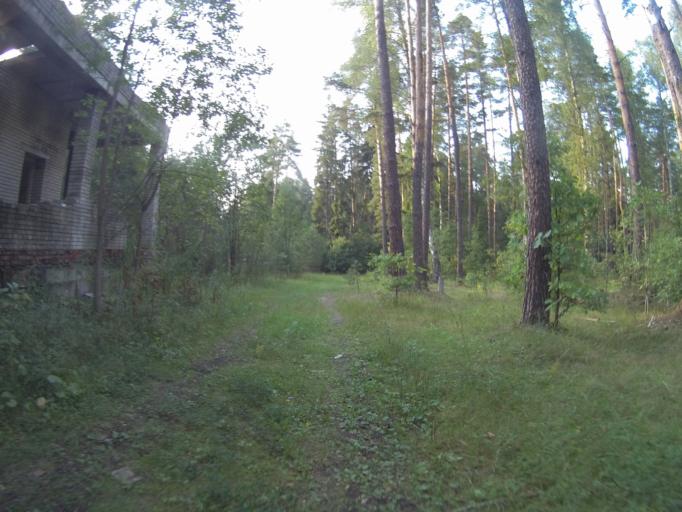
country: RU
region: Vladimir
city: Kommunar
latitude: 56.0629
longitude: 40.4614
